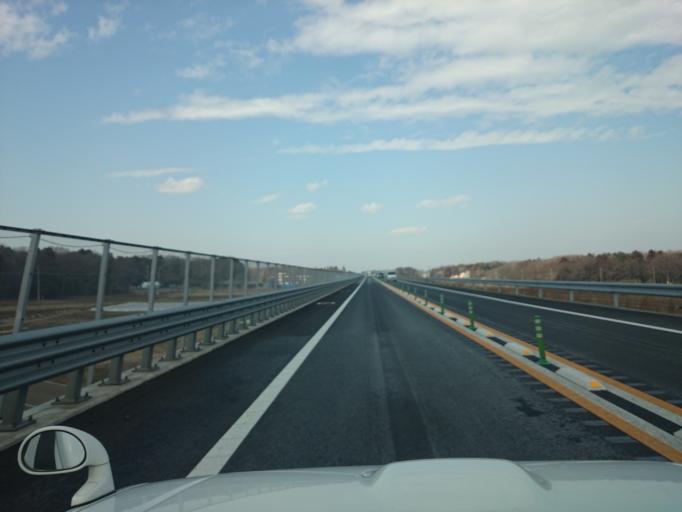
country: JP
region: Ibaraki
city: Iwai
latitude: 36.0999
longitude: 139.8672
